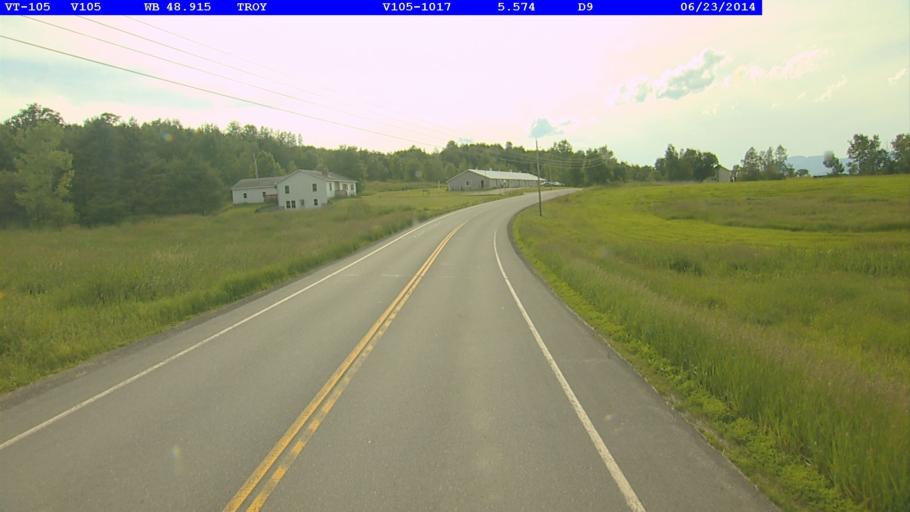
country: US
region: Vermont
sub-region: Orleans County
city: Newport
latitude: 44.9802
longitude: -72.3508
